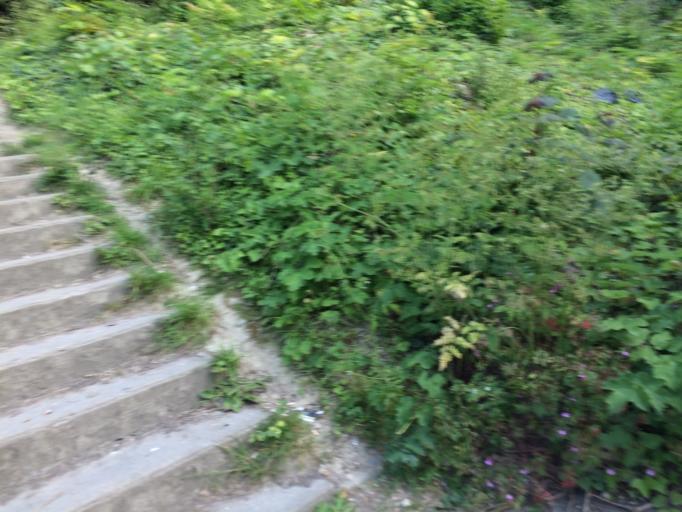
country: FR
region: Ile-de-France
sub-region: Departement de l'Essonne
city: Grigny
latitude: 48.6529
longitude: 2.3960
